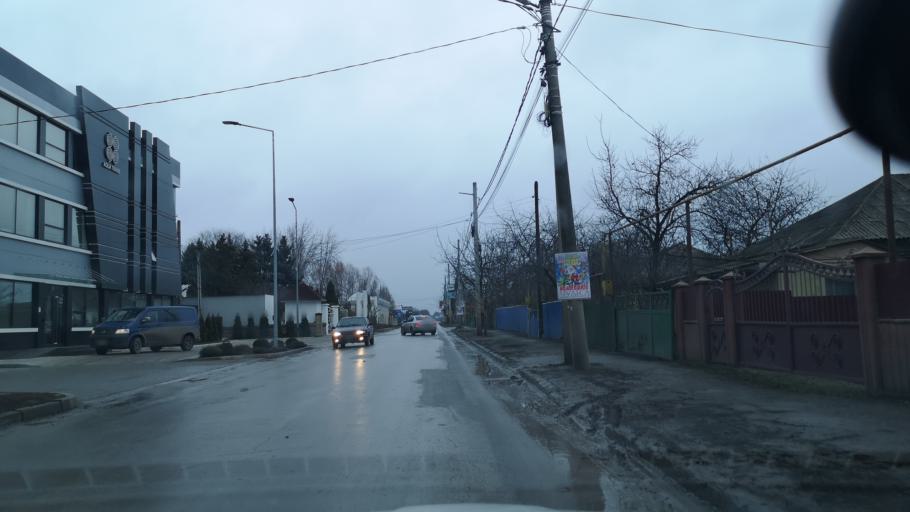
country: MD
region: Balti
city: Balti
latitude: 47.7783
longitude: 27.9465
